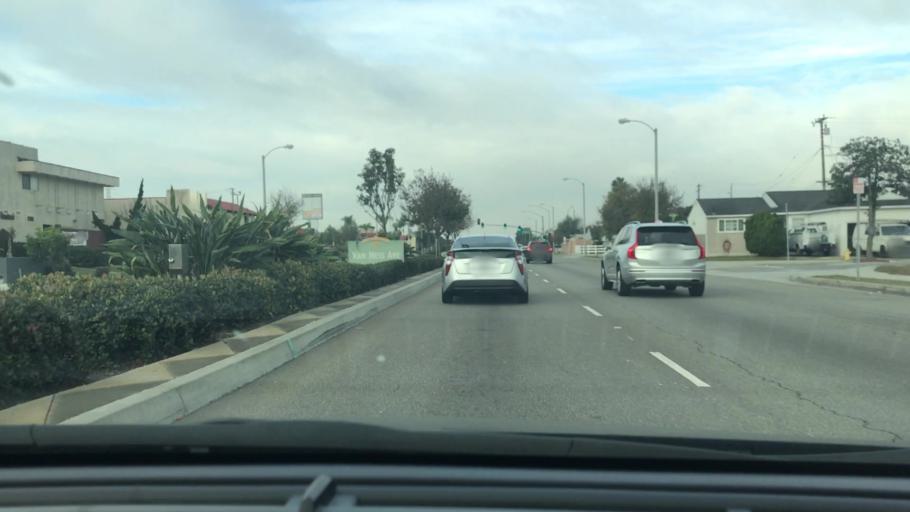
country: US
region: California
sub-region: Los Angeles County
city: Gardena
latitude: 33.8729
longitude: -118.3157
